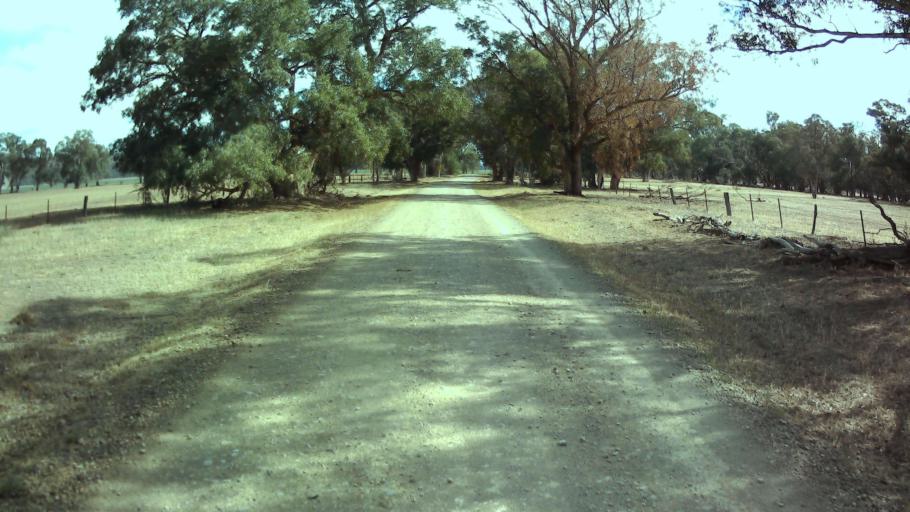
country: AU
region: New South Wales
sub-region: Weddin
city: Grenfell
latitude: -33.6896
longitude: 148.3045
